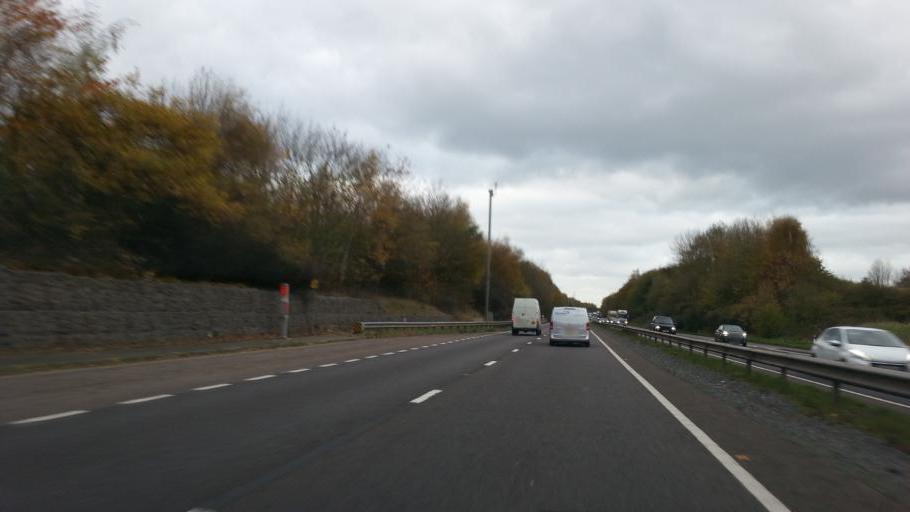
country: GB
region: England
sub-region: Derbyshire
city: Melbourne
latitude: 52.7768
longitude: -1.4199
